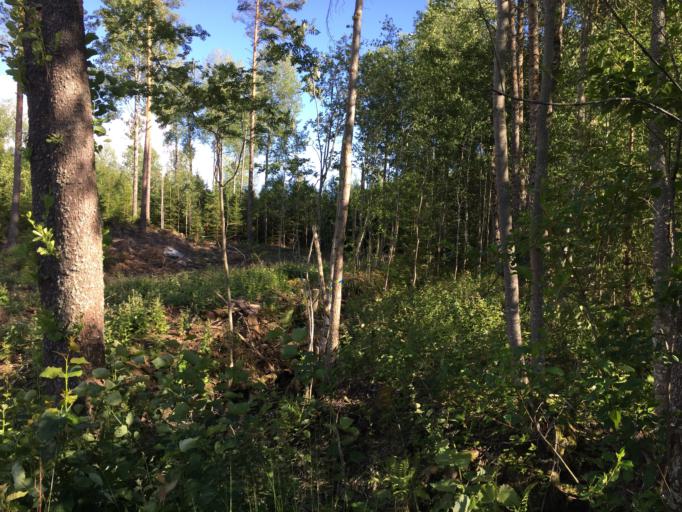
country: SE
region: Soedermanland
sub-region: Vingakers Kommun
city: Vingaker
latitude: 58.9895
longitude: 15.6872
